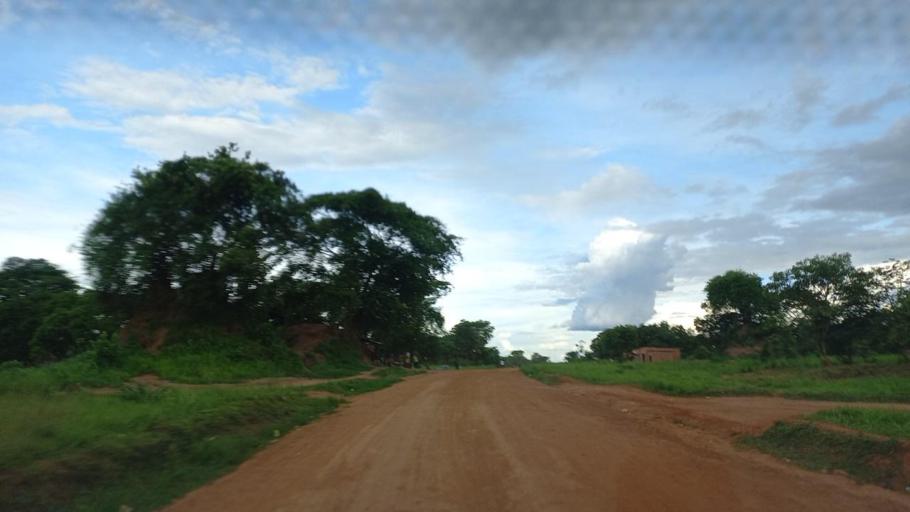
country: ZM
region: North-Western
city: Mwinilunga
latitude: -11.7586
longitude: 24.4218
